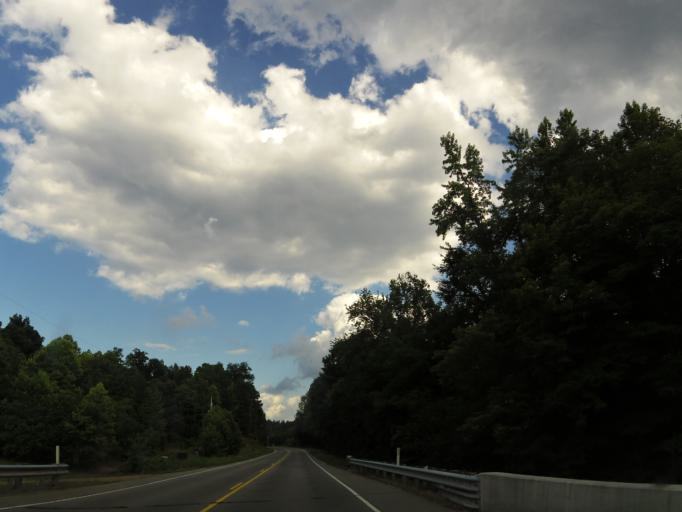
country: US
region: Tennessee
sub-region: Lewis County
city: Hohenwald
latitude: 35.5890
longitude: -87.6859
